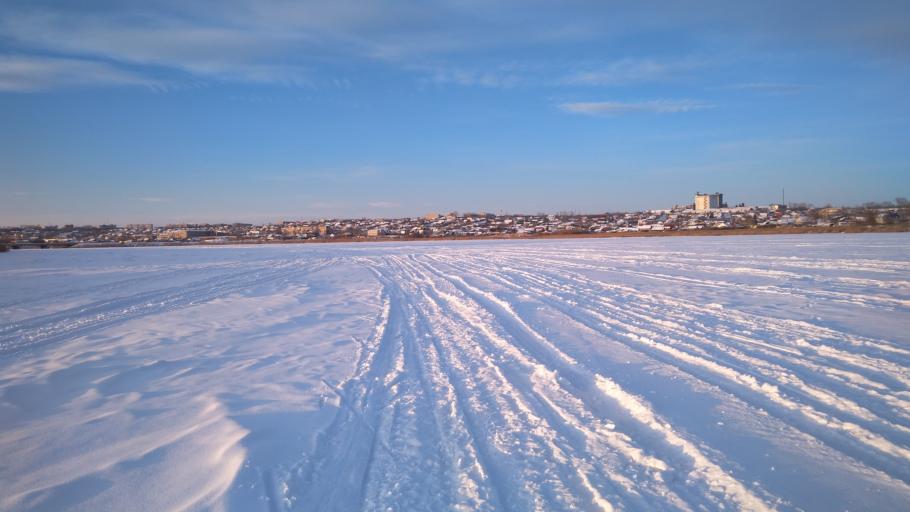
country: RU
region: Chelyabinsk
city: Troitsk
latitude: 54.0865
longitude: 61.5862
